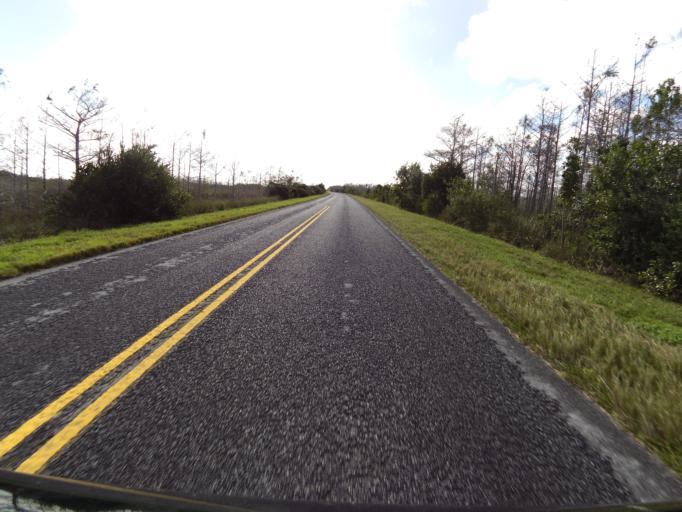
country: US
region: Florida
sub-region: Miami-Dade County
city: Florida City
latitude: 25.4222
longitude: -80.7766
